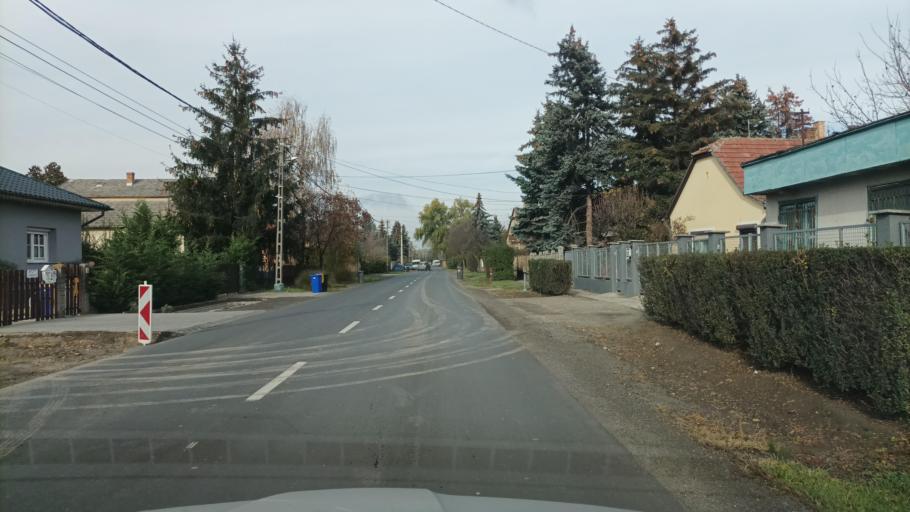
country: HU
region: Pest
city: Rackeve
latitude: 47.1445
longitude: 18.9469
